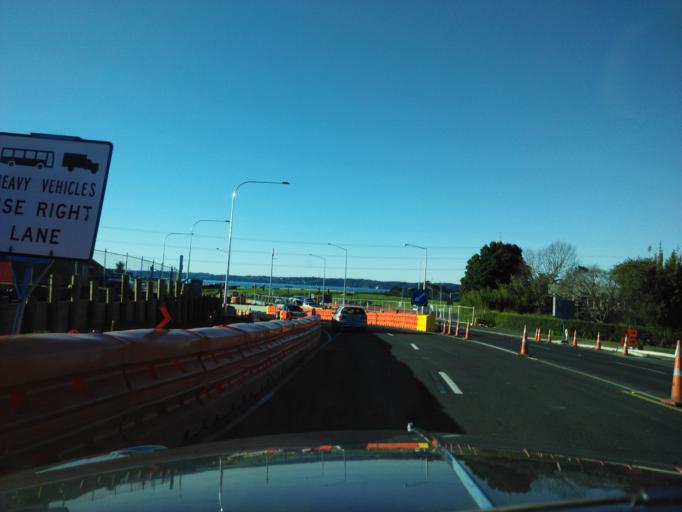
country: NZ
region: Auckland
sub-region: Auckland
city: Rosebank
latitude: -36.8595
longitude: 174.6517
